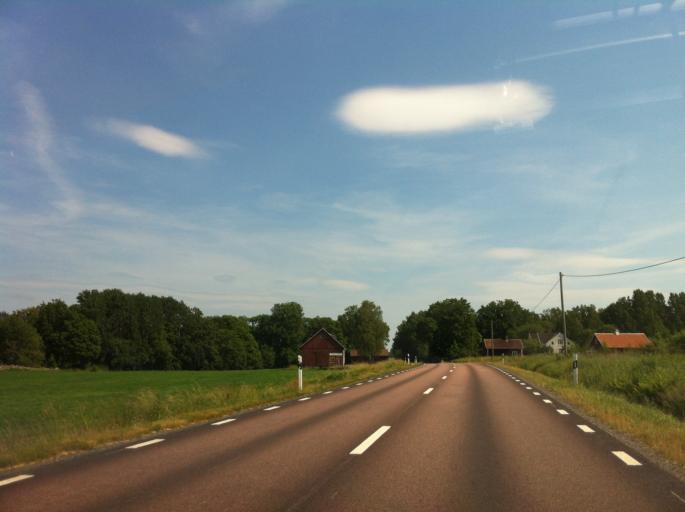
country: SE
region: Kalmar
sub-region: Nybro Kommun
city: Nybro
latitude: 56.7899
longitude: 15.7953
